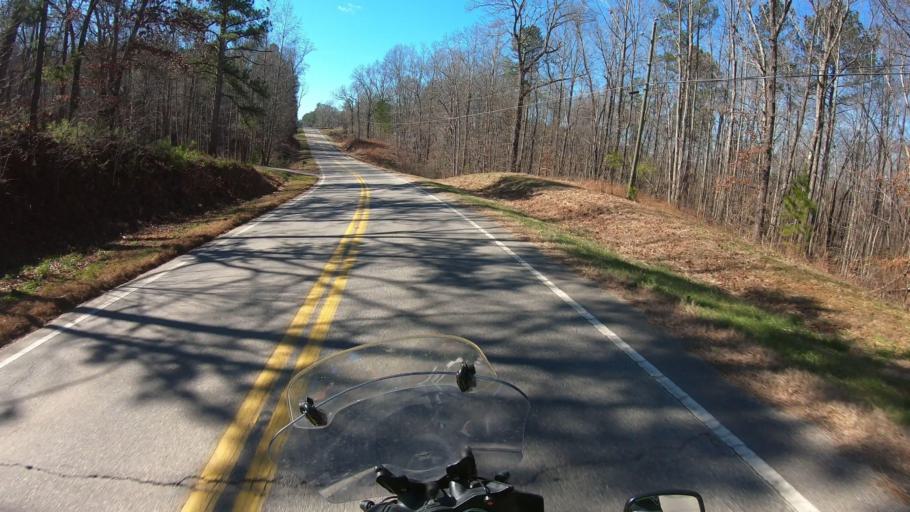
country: US
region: Georgia
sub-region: Haralson County
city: Tallapoosa
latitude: 33.7386
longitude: -85.4204
